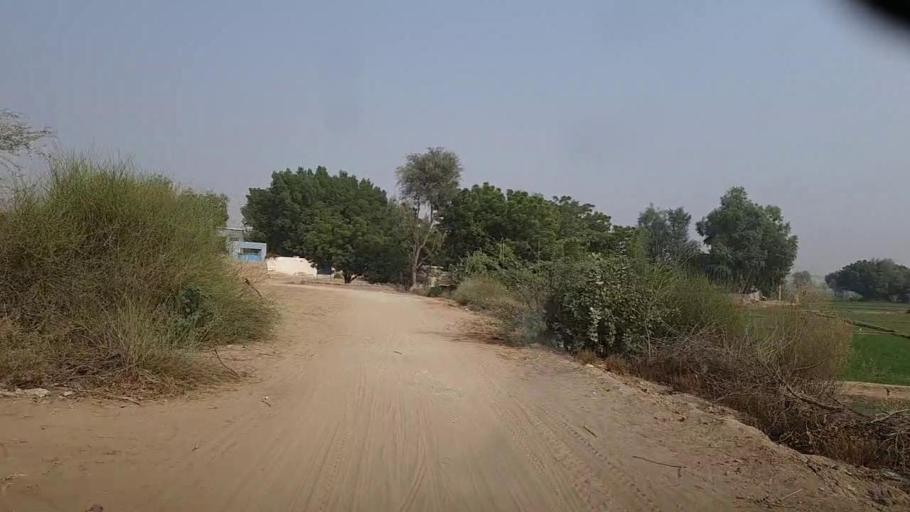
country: PK
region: Sindh
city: Bozdar
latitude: 27.0586
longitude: 68.6615
